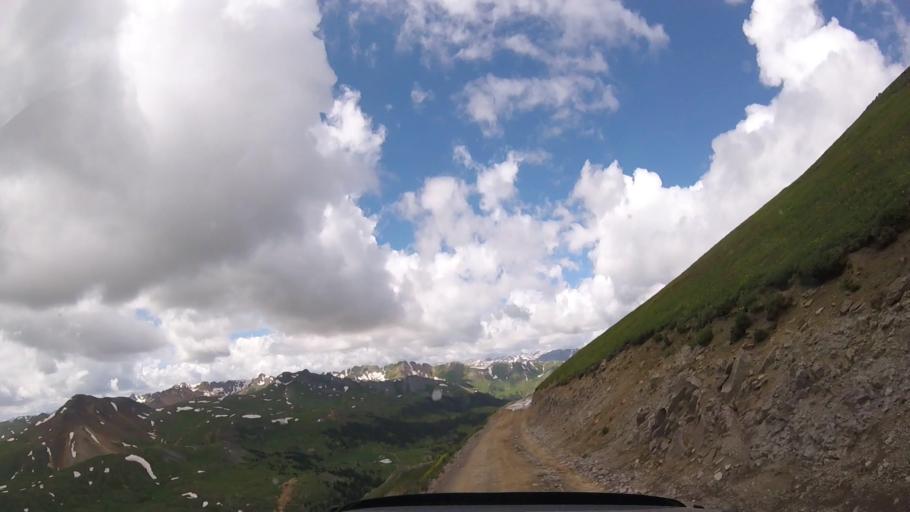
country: US
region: Colorado
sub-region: Ouray County
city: Ouray
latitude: 37.9658
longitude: -107.5821
